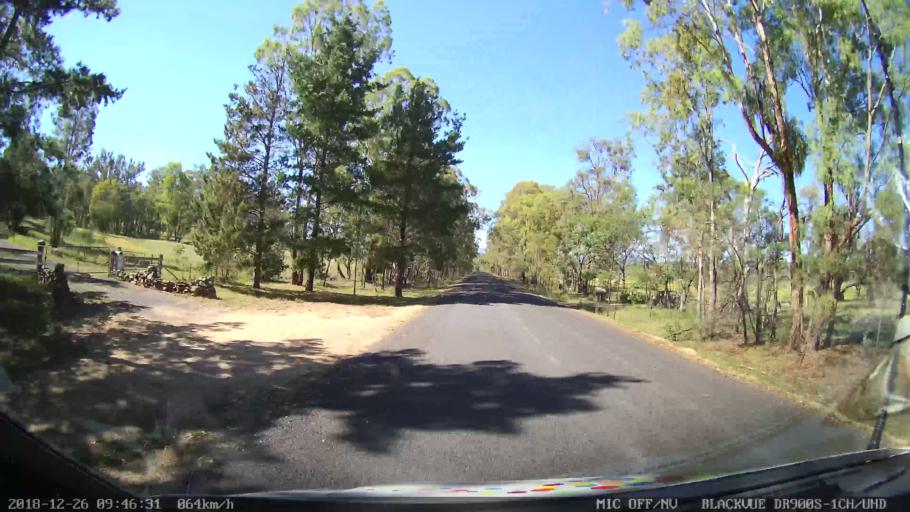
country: AU
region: New South Wales
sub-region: Mid-Western Regional
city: Kandos
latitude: -32.9705
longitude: 150.1051
